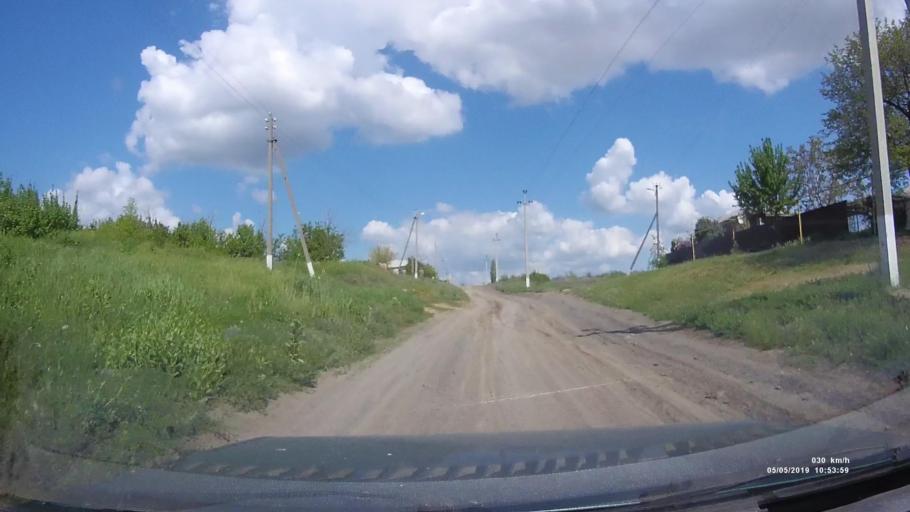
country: RU
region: Rostov
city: Ust'-Donetskiy
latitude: 47.6562
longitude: 40.8236
